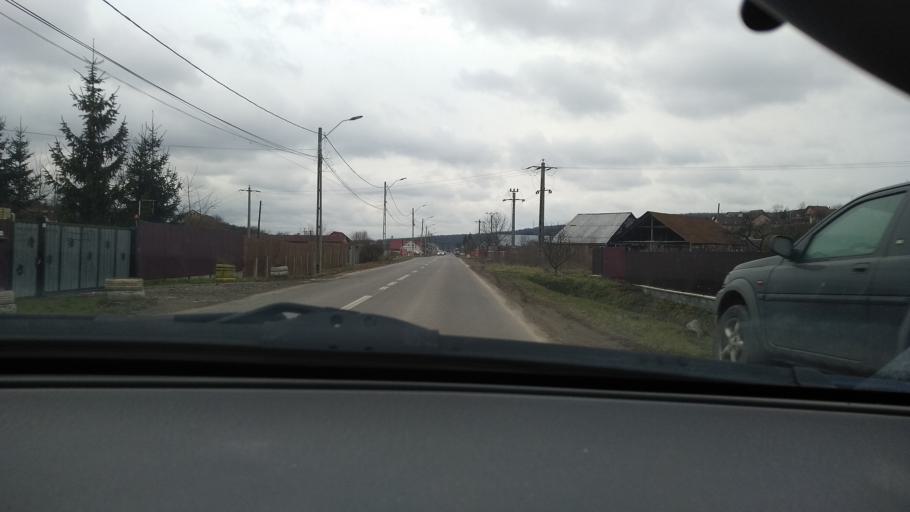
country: RO
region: Mures
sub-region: Comuna Livezeni
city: Livezeni
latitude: 46.5471
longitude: 24.6333
